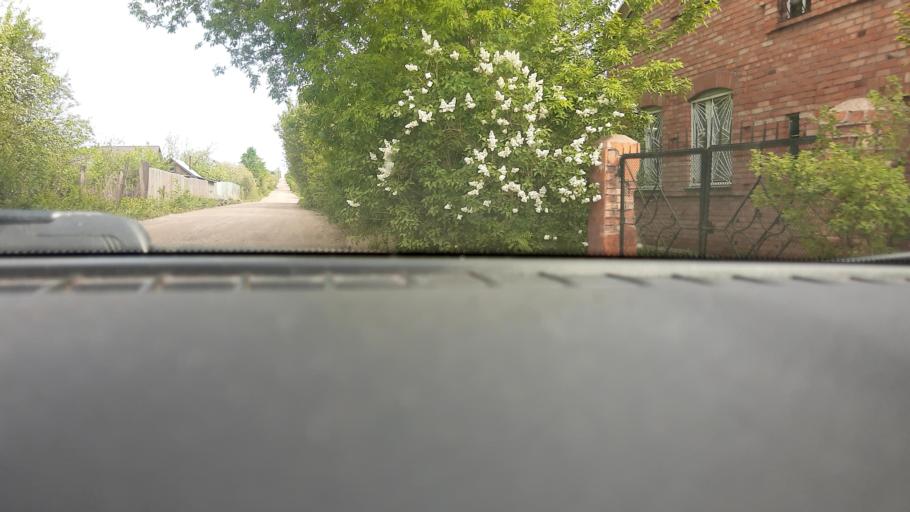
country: RU
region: Bashkortostan
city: Avdon
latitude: 54.5691
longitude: 55.7409
